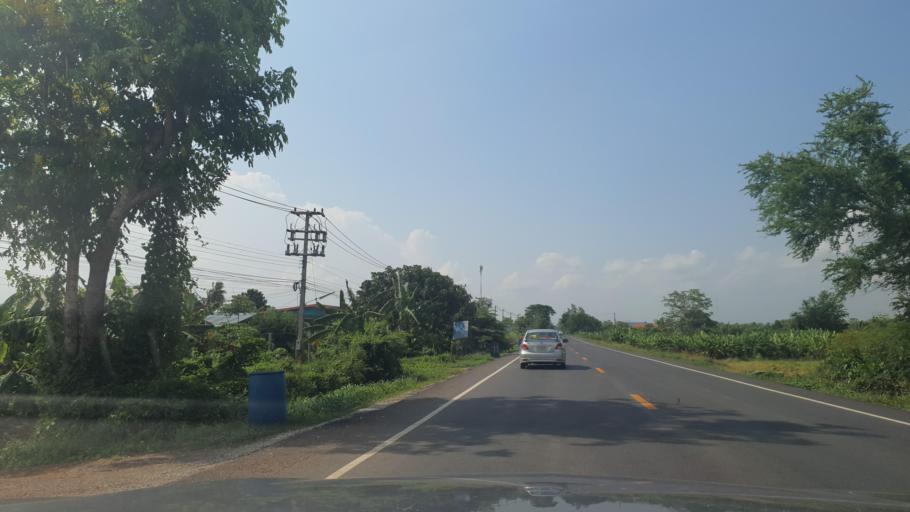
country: TH
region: Sukhothai
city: Si Samrong
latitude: 17.2054
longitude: 99.8491
